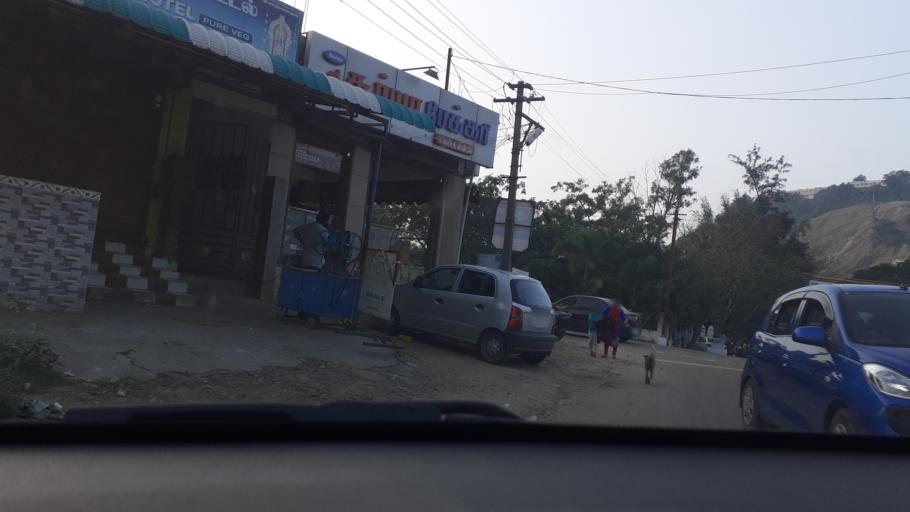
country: IN
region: Tamil Nadu
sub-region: Dindigul
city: Palani
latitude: 10.4325
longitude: 77.5235
